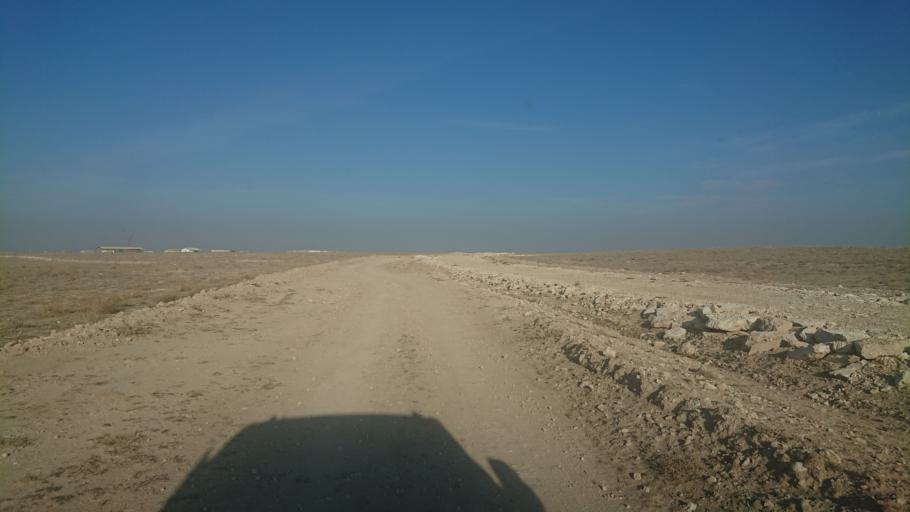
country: TR
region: Aksaray
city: Sultanhani
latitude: 38.1426
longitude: 33.5749
